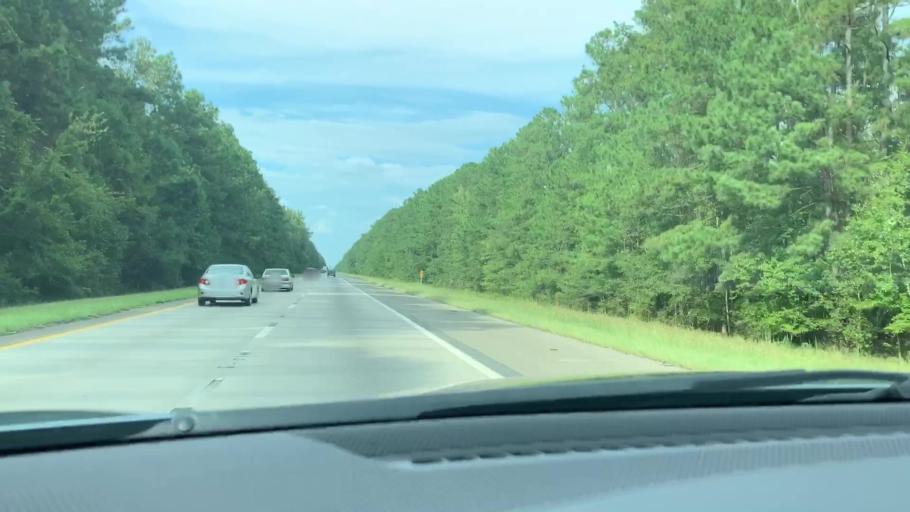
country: US
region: South Carolina
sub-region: Colleton County
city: Walterboro
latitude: 32.9678
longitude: -80.6766
